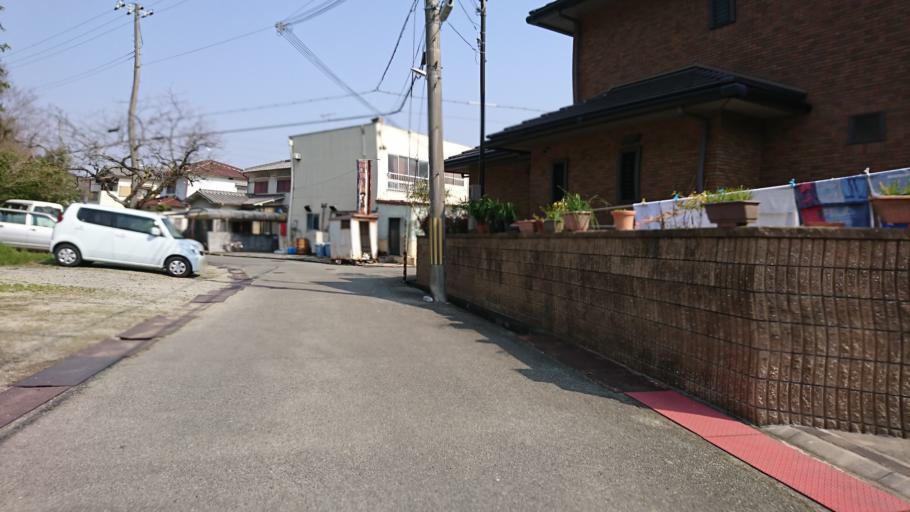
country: JP
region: Hyogo
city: Shirahamacho-usazakiminami
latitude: 34.7852
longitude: 134.7669
